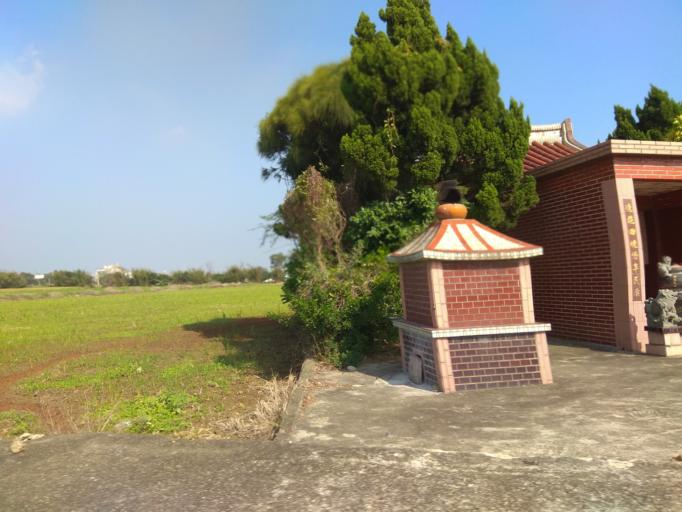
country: TW
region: Taiwan
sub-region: Hsinchu
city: Zhubei
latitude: 24.9972
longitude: 121.0614
